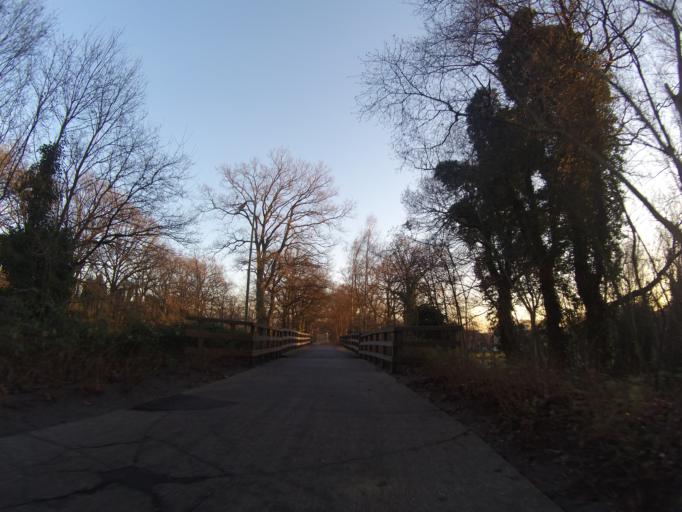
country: NL
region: Drenthe
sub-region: Gemeente Emmen
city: Emmen
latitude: 52.7555
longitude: 6.8949
